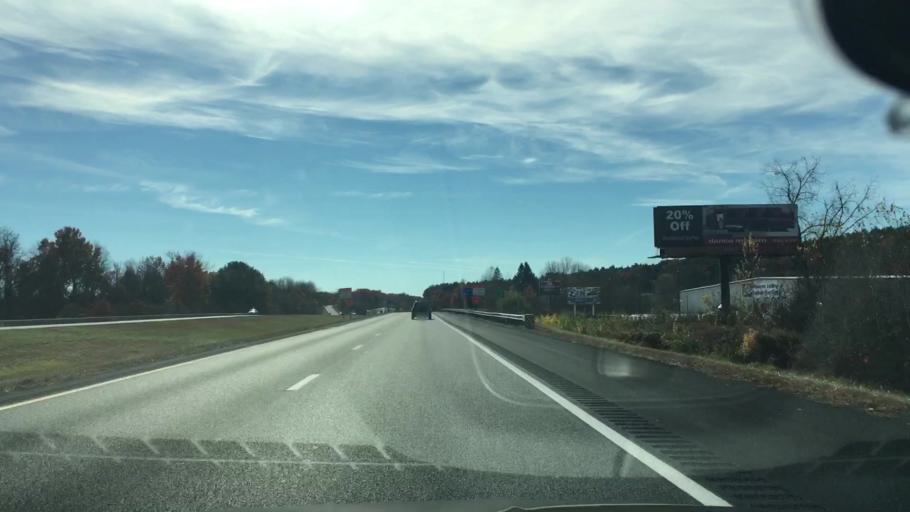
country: US
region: Massachusetts
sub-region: Hampshire County
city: Hatfield
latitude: 42.3685
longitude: -72.6347
